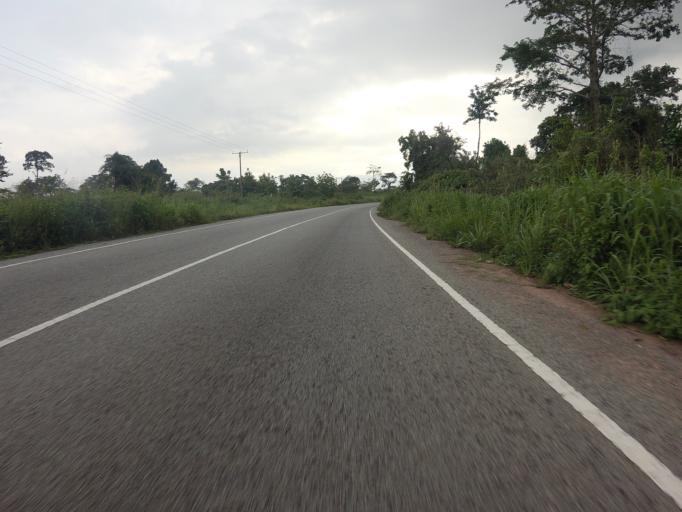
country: GH
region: Volta
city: Ho
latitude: 6.7835
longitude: 0.4595
